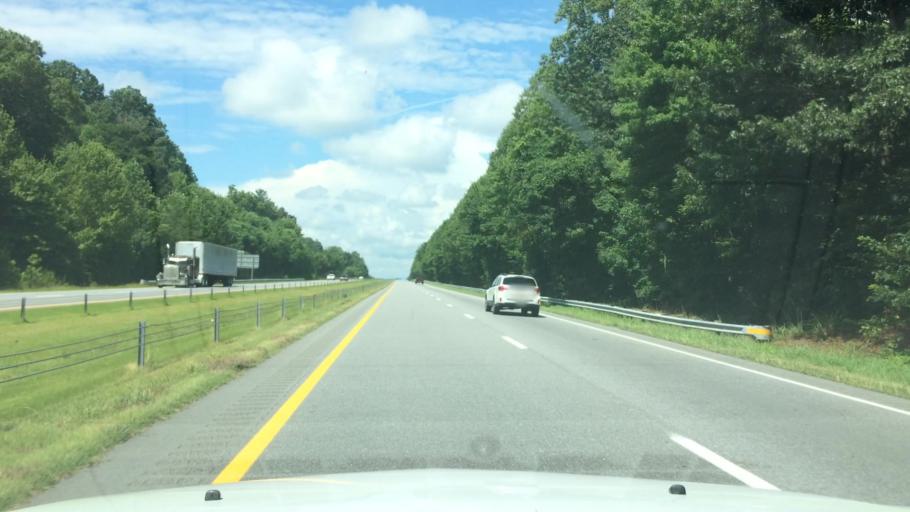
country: US
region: North Carolina
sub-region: Wilkes County
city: North Wilkesboro
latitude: 36.1482
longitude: -81.0363
